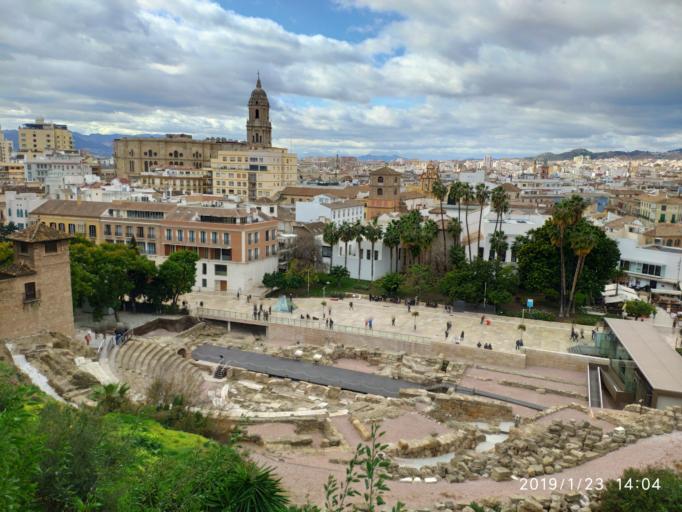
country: ES
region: Andalusia
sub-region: Provincia de Malaga
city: Malaga
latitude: 36.7214
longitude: -4.4161
